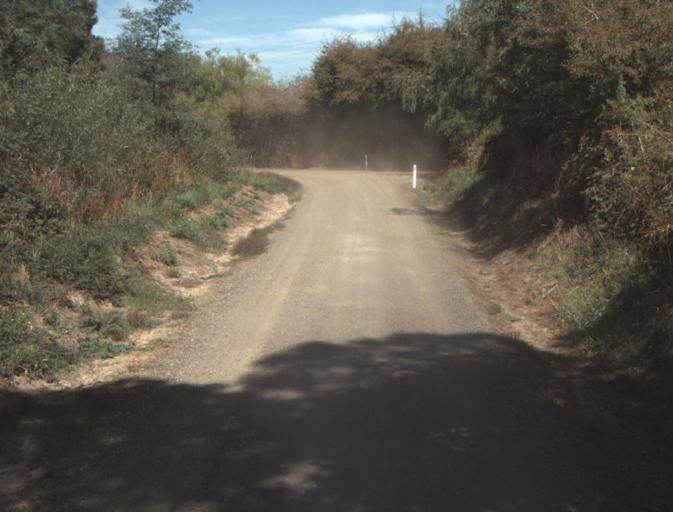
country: AU
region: Tasmania
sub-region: Launceston
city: Mayfield
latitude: -41.2569
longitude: 147.1701
